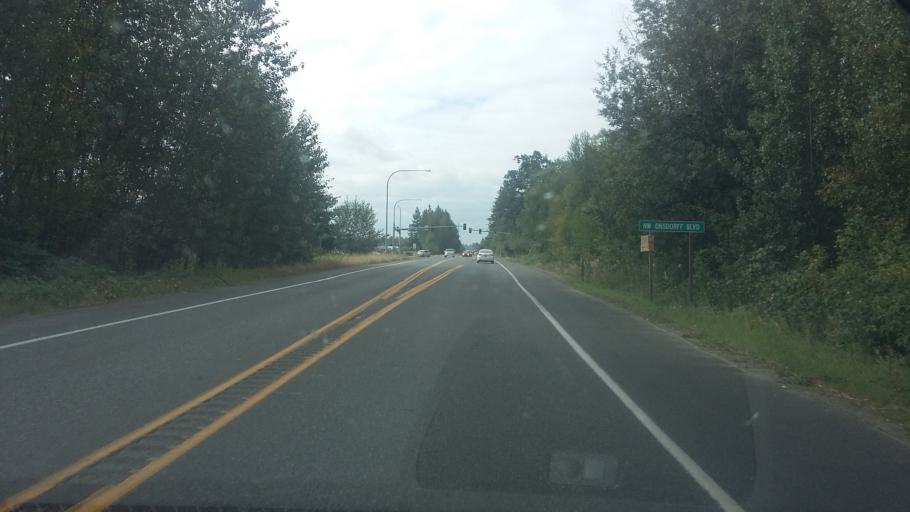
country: US
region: Washington
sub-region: Clark County
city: Battle Ground
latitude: 45.7935
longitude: -122.5475
